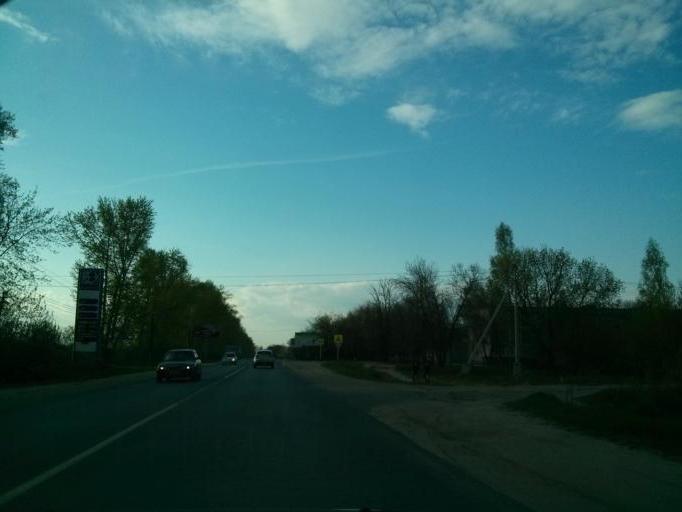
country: RU
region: Vladimir
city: Murom
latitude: 55.5977
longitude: 42.0333
